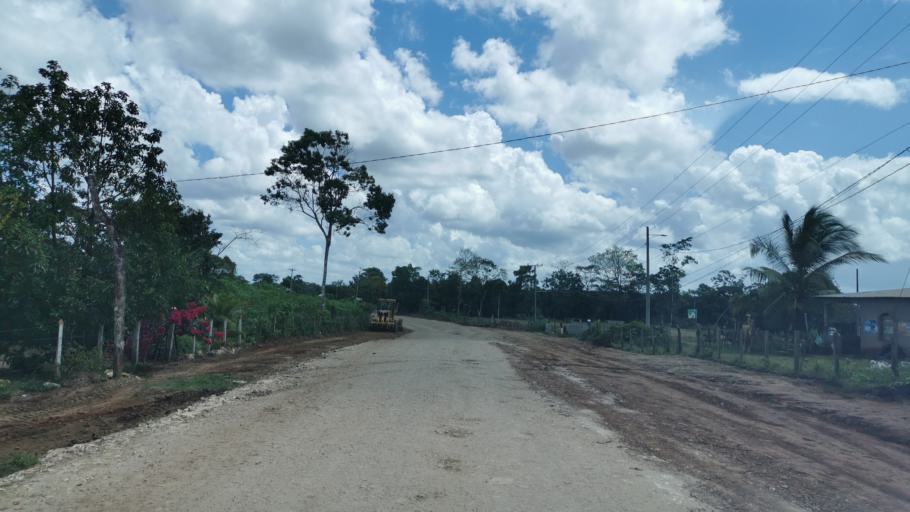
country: NI
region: Atlantico Sur
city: Rama
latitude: 12.2281
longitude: -84.2336
